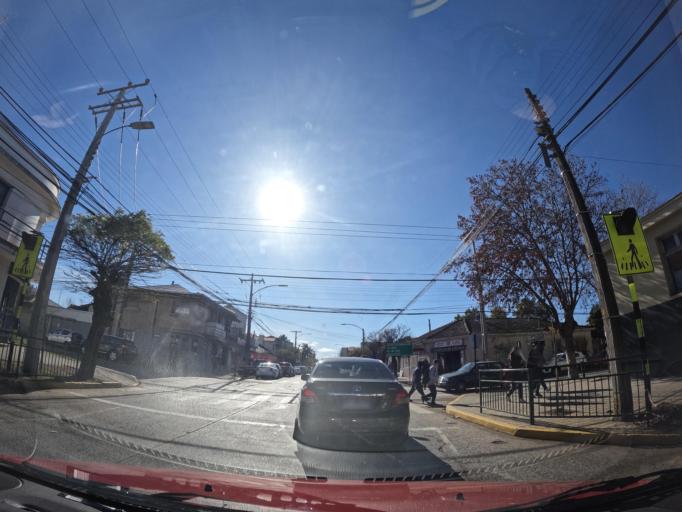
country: CL
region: Maule
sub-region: Provincia de Cauquenes
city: Cauquenes
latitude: -35.9690
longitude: -72.3147
